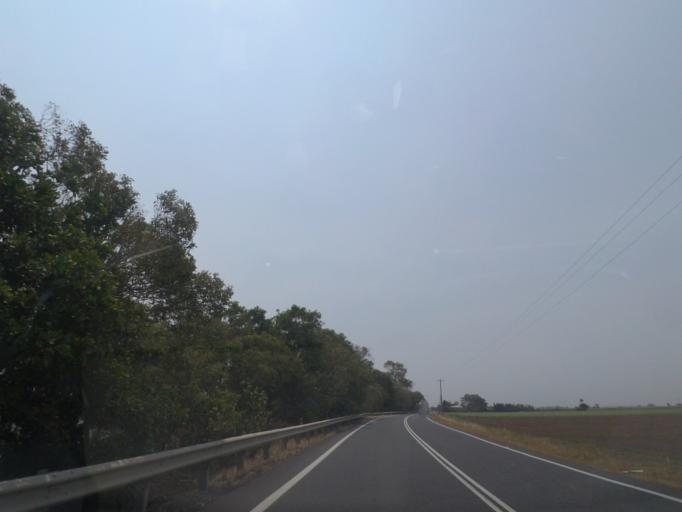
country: AU
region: New South Wales
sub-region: Richmond Valley
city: Evans Head
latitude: -28.9728
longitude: 153.4606
